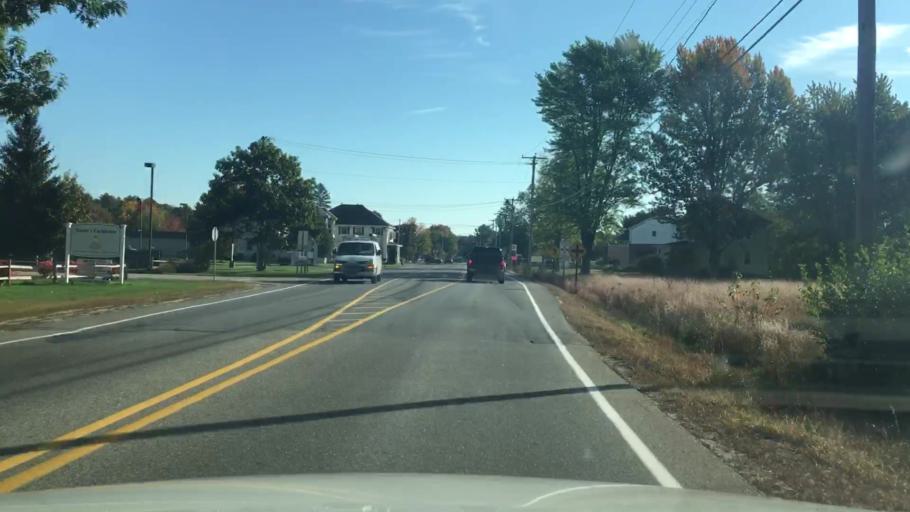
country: US
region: Maine
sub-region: Cumberland County
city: Westbrook
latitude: 43.6418
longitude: -70.4003
